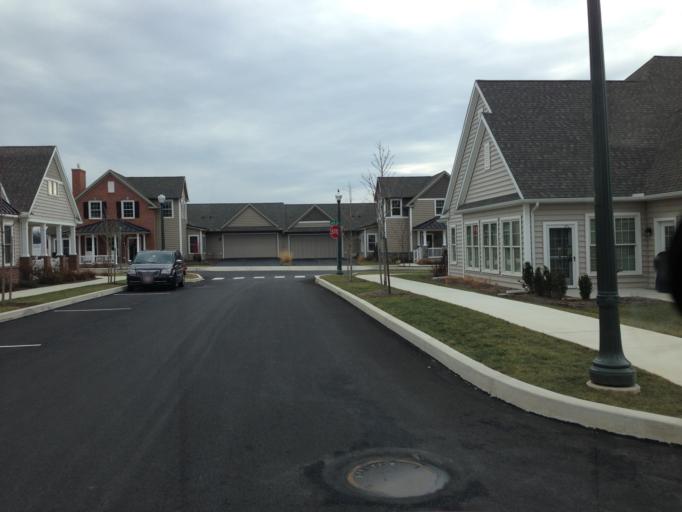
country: US
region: Pennsylvania
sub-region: Lancaster County
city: Lititz
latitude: 40.1480
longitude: -76.3171
